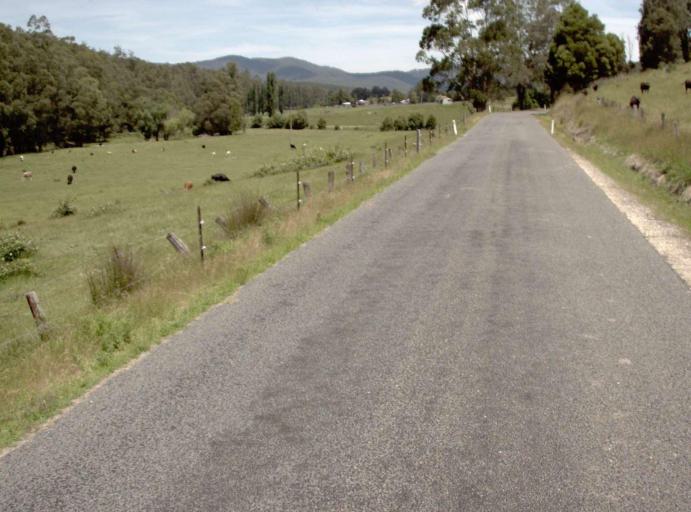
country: AU
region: New South Wales
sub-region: Bombala
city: Bombala
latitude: -37.3744
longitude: 149.0141
